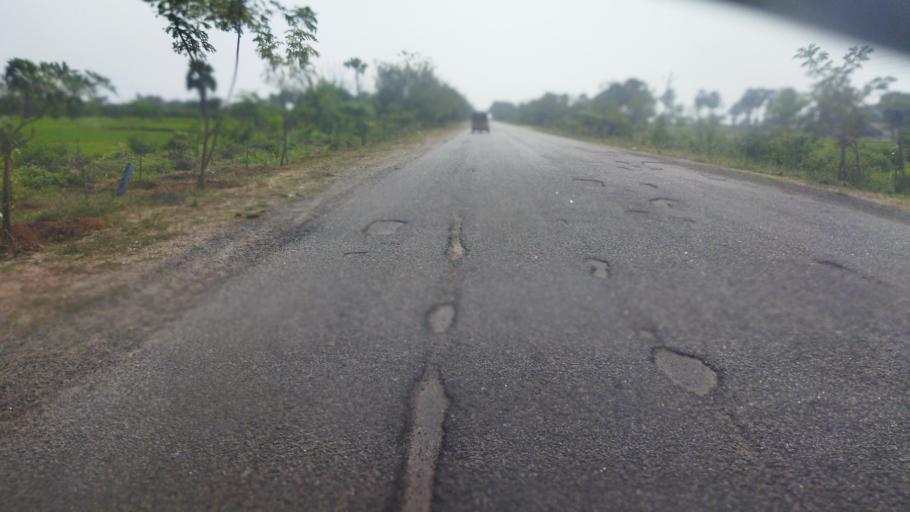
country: IN
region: Telangana
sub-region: Nalgonda
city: Nalgonda
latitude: 17.1056
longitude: 79.2809
